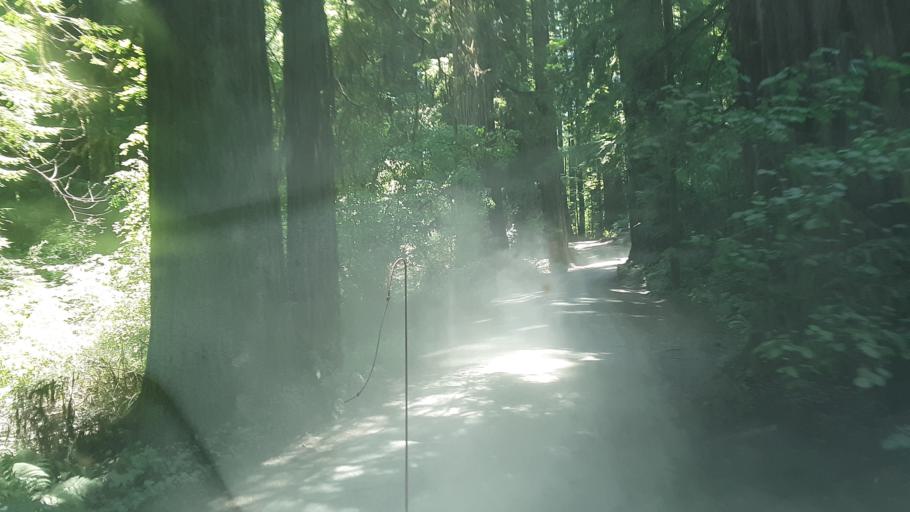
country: US
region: California
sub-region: Del Norte County
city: Bertsch-Oceanview
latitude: 41.8178
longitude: -124.1118
